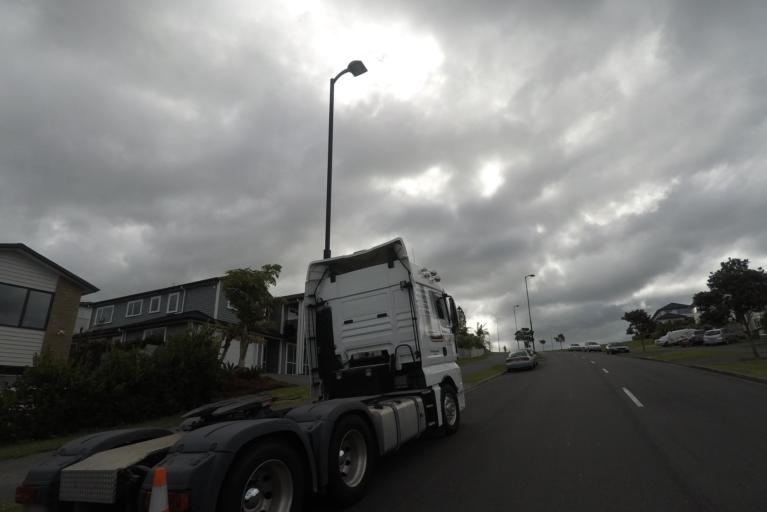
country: NZ
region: Auckland
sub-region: Auckland
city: Rothesay Bay
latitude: -36.6047
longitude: 174.6756
